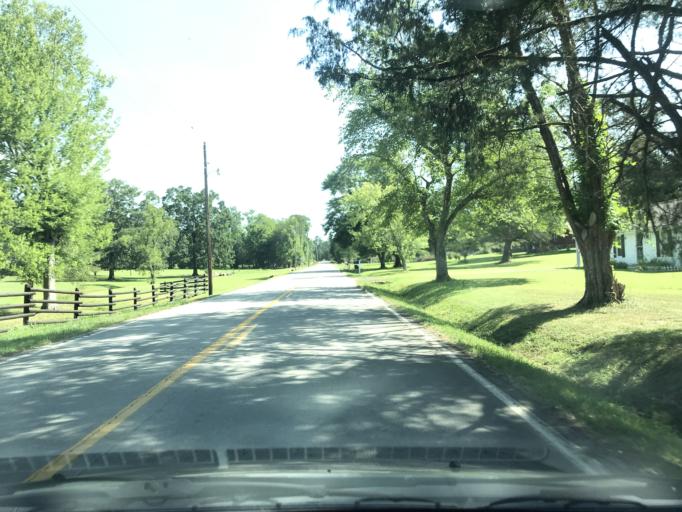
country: US
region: Tennessee
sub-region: Hamilton County
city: Sale Creek
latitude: 35.3350
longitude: -85.0068
